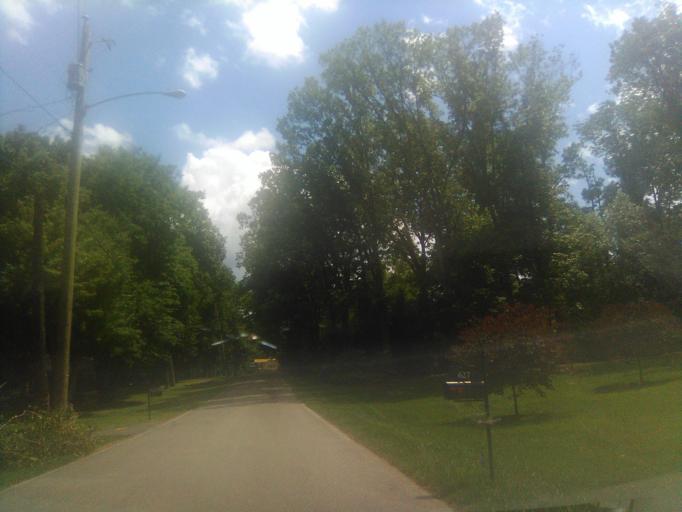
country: US
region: Tennessee
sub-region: Davidson County
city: Belle Meade
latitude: 36.0992
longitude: -86.8480
